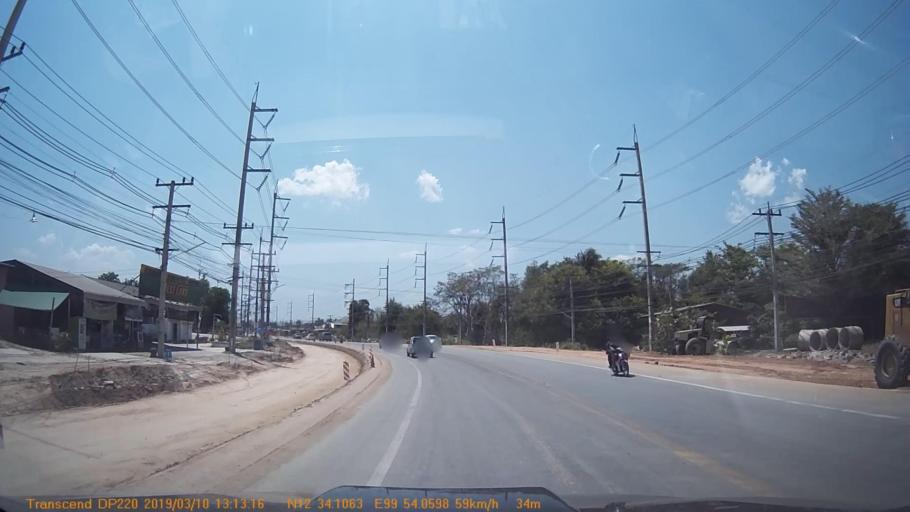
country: TH
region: Prachuap Khiri Khan
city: Hua Hin
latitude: 12.5684
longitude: 99.9009
